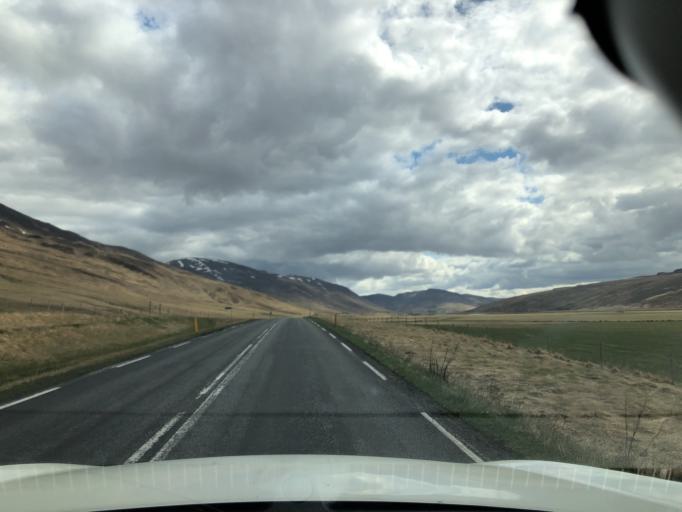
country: IS
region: Northwest
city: Saudarkrokur
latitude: 65.5712
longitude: -19.9892
